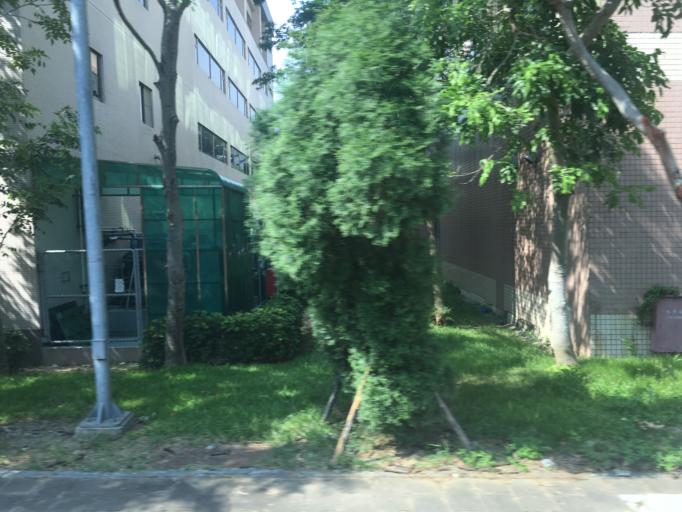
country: TW
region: Taiwan
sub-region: Hsinchu
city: Hsinchu
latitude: 24.7742
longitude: 121.0072
